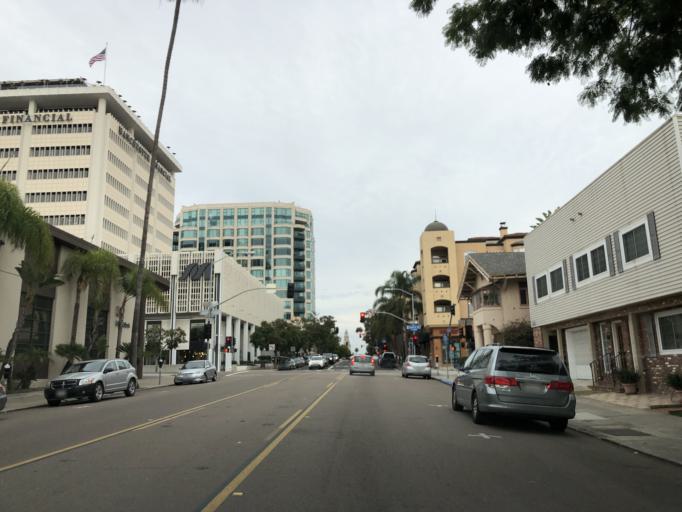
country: US
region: California
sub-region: San Diego County
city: San Diego
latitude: 32.7314
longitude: -117.1619
